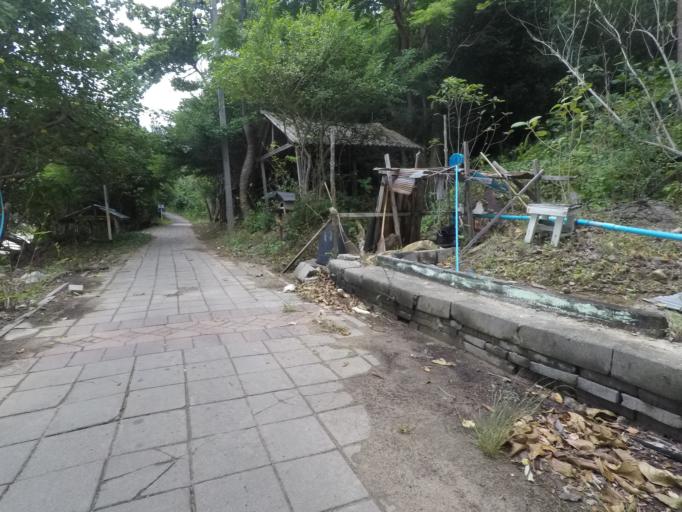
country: TH
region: Phangnga
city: Ban Phru Nai
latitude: 7.7707
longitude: 98.7676
